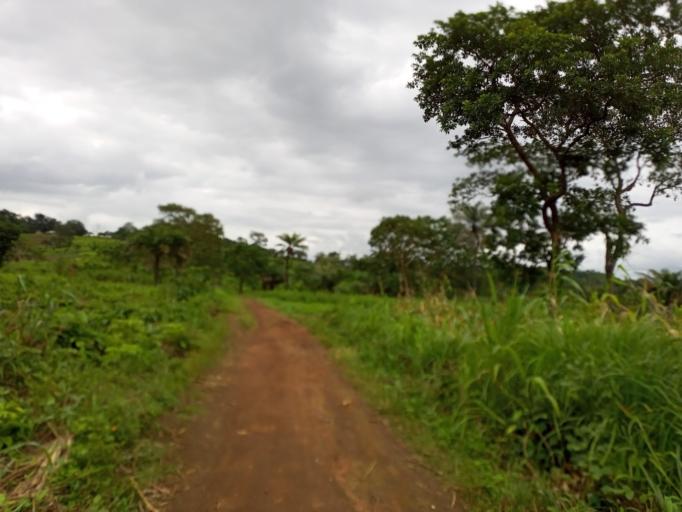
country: SL
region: Northern Province
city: Kamakwie
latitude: 9.5039
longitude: -12.2690
